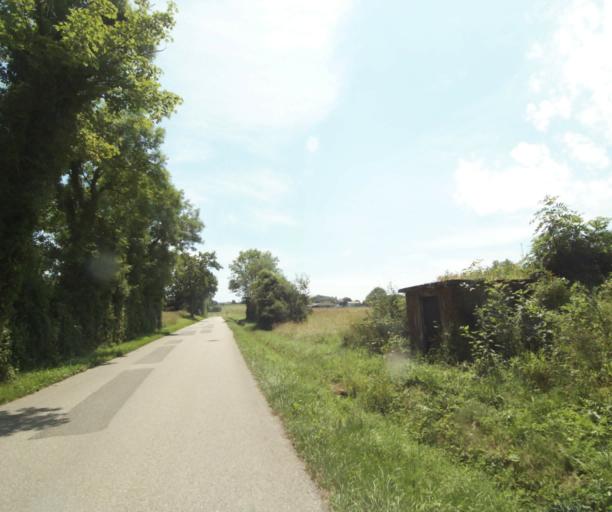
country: FR
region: Rhone-Alpes
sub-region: Departement de la Haute-Savoie
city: Messery
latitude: 46.3626
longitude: 6.3106
